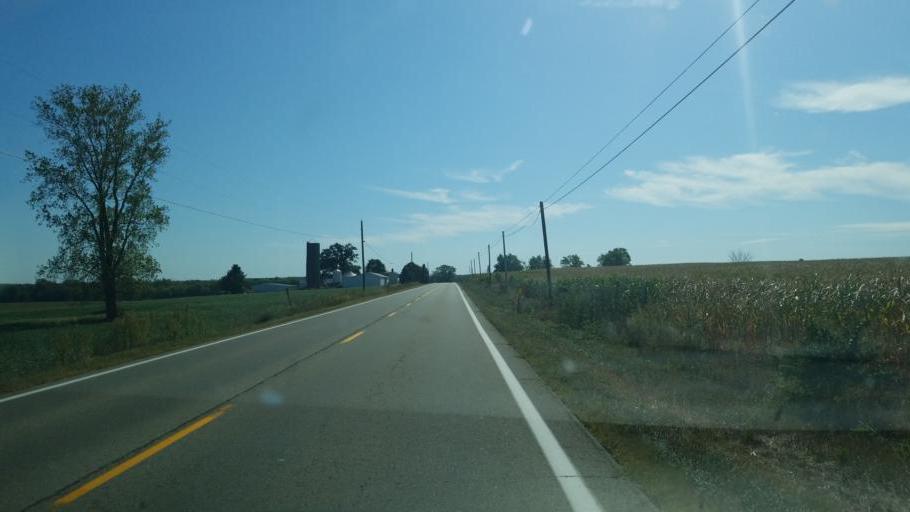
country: US
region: Ohio
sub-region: Champaign County
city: Mechanicsburg
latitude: 40.0861
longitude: -83.5367
